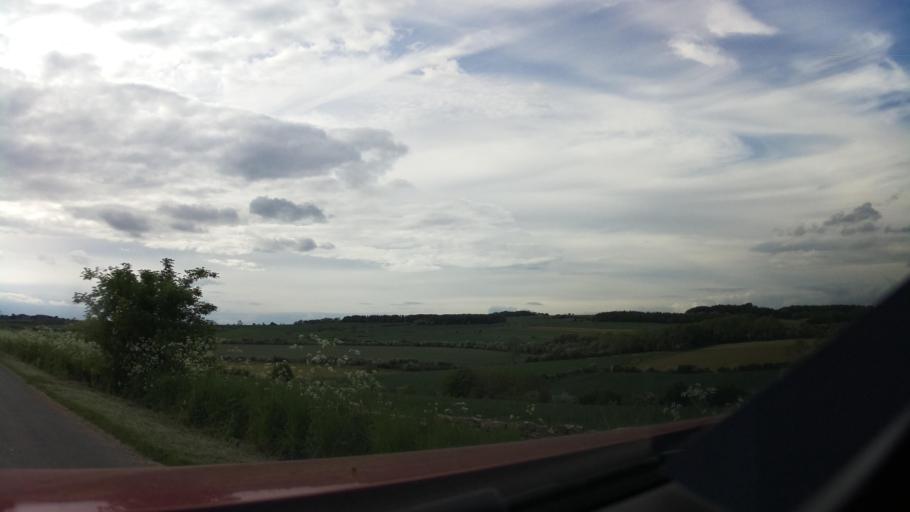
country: GB
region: England
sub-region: Gloucestershire
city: Shipton Village
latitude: 51.8753
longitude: -1.9293
